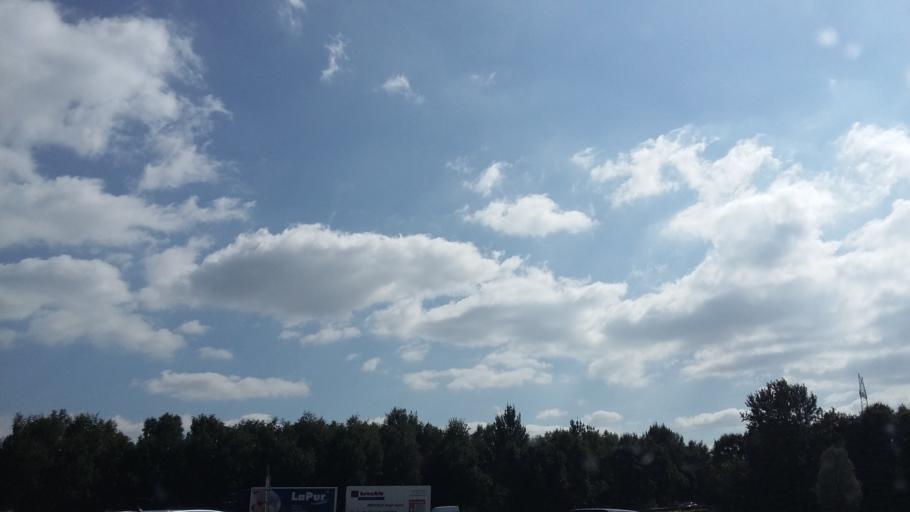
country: DE
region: Bremen
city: Bremen
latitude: 53.1173
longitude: 8.8138
